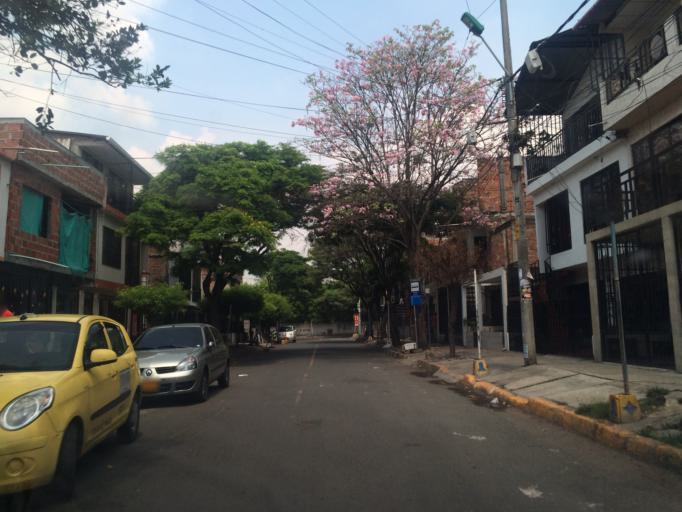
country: CO
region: Valle del Cauca
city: Cali
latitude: 3.4938
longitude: -76.4891
